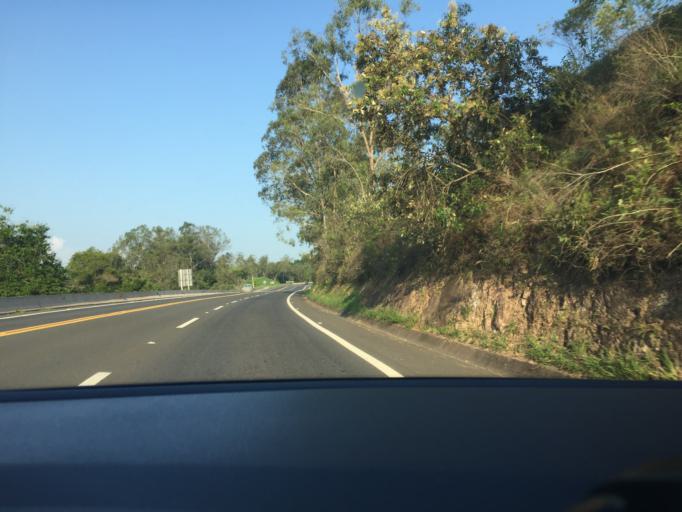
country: BR
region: Sao Paulo
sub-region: Louveira
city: Louveira
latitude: -23.0825
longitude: -46.9221
